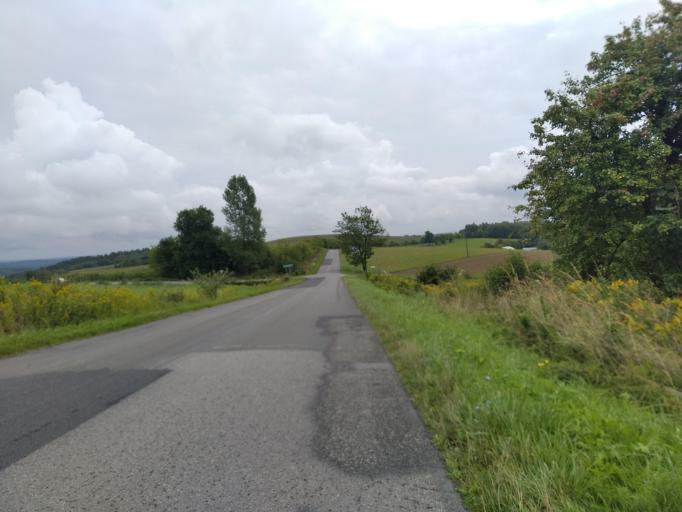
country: PL
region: Subcarpathian Voivodeship
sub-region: Powiat przemyski
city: Dubiecko
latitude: 49.7182
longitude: 22.3207
